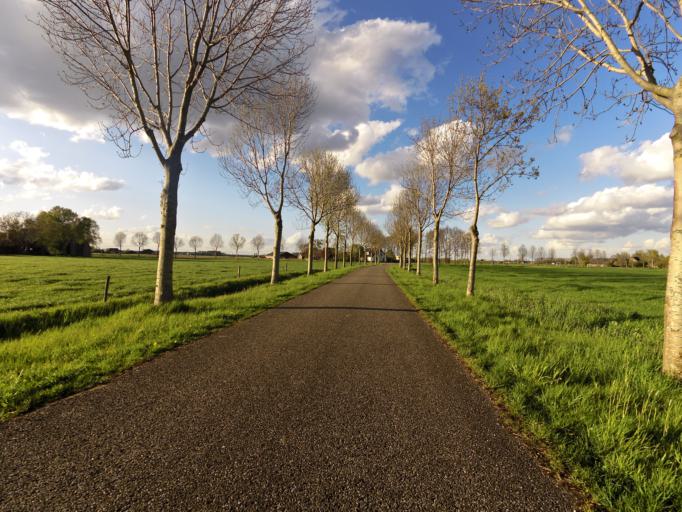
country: NL
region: Gelderland
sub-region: Gemeente Doesburg
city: Doesburg
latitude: 51.9575
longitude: 6.1254
